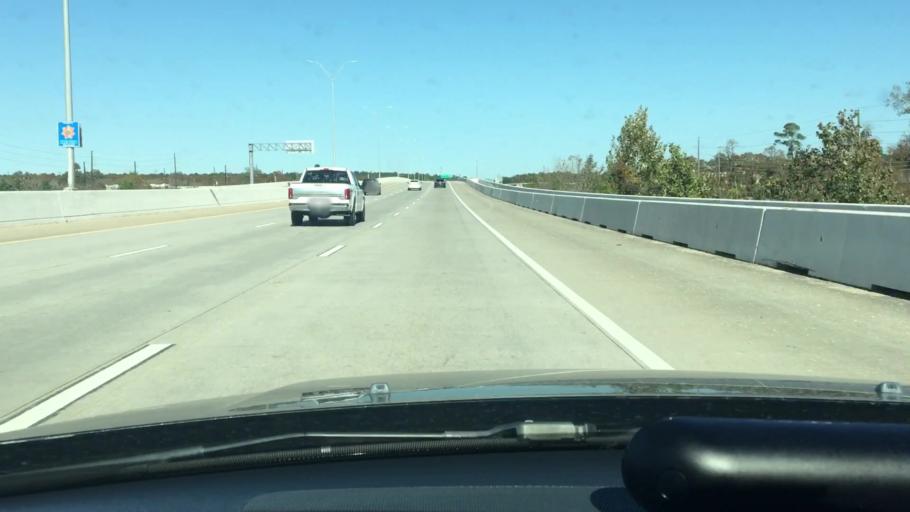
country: US
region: Texas
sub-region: Harris County
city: Sheldon
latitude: 29.8935
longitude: -95.2029
